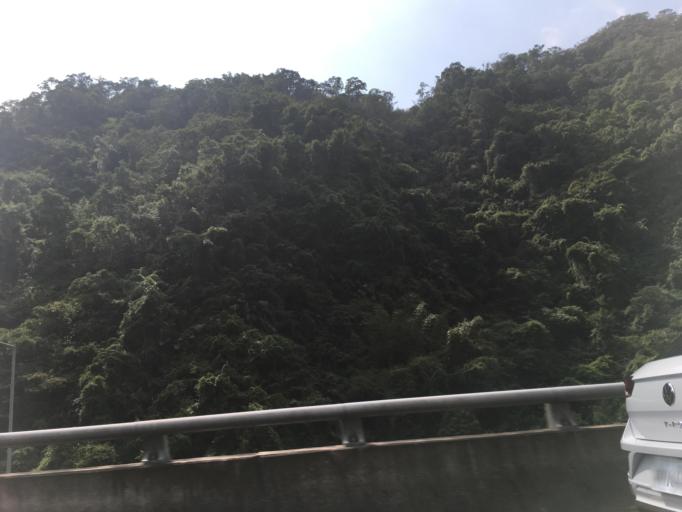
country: TW
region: Taiwan
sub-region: Keelung
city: Keelung
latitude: 24.9462
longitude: 121.7091
